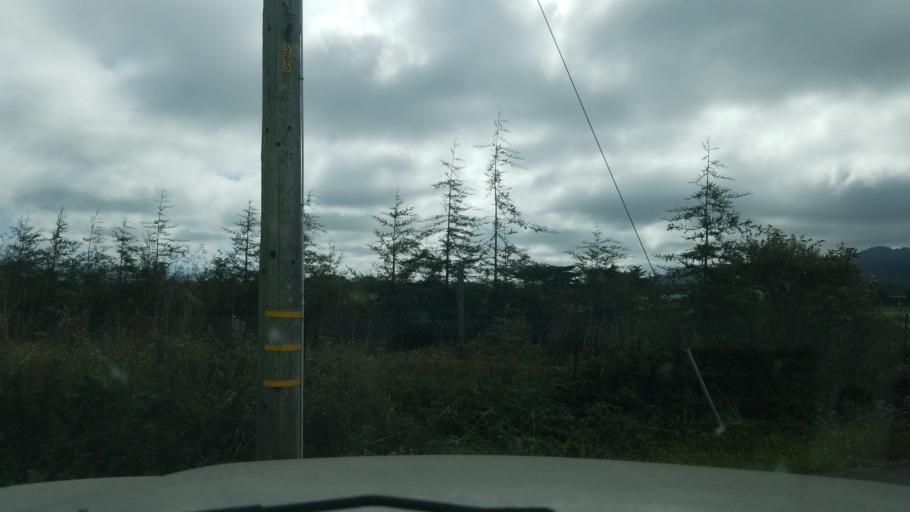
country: US
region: California
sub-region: Humboldt County
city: Ferndale
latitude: 40.5897
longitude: -124.2552
